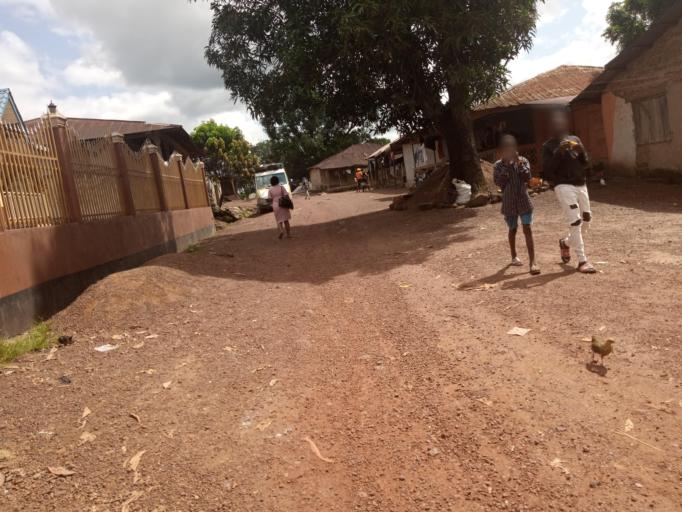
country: SL
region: Northern Province
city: Kamakwie
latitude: 9.4967
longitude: -12.2419
